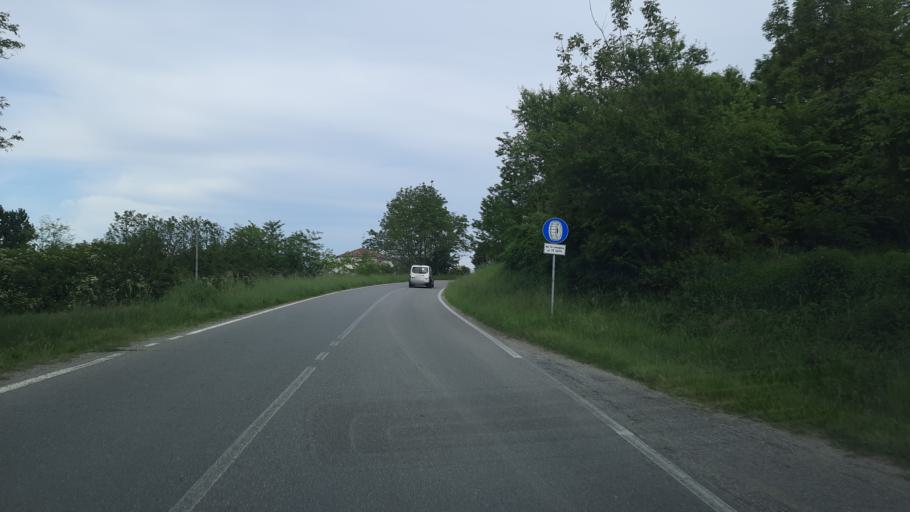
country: IT
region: Piedmont
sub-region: Provincia di Alessandria
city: Coniolo Bricco
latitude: 45.1403
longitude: 8.3852
